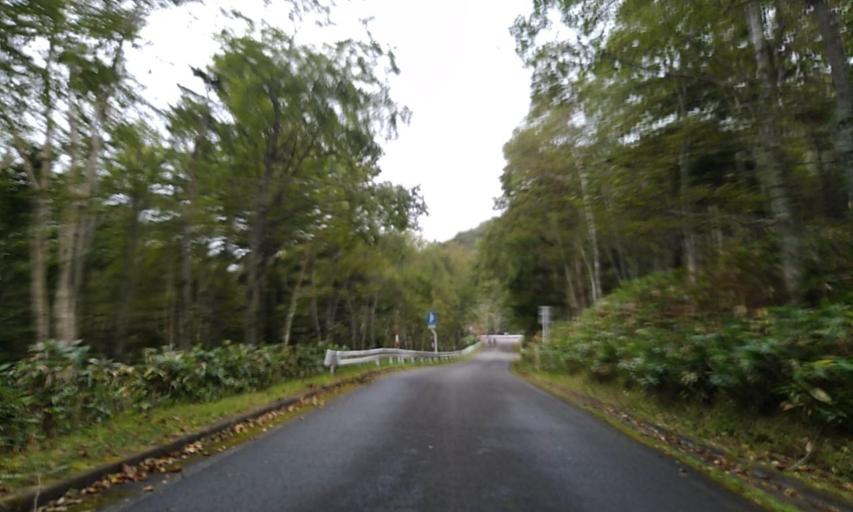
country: JP
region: Hokkaido
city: Bihoro
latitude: 43.5811
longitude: 144.2337
